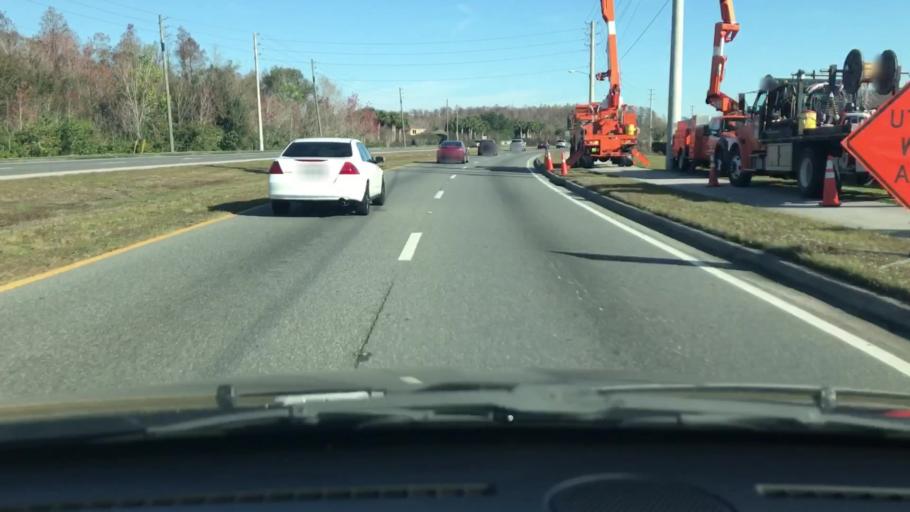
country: US
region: Florida
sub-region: Osceola County
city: Campbell
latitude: 28.2224
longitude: -81.4401
